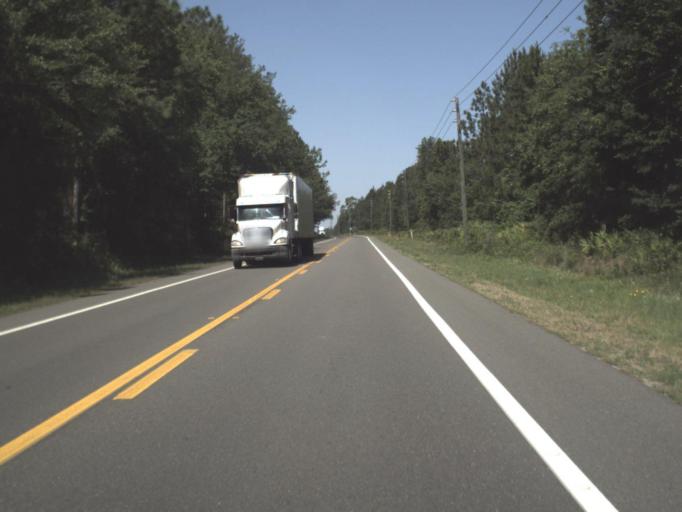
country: US
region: Florida
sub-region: Baker County
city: Macclenny
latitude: 30.2910
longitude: -82.0702
